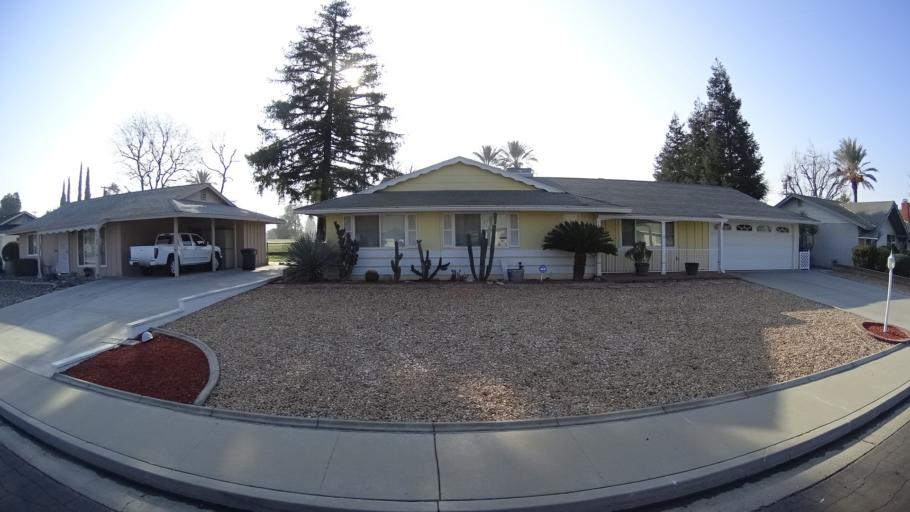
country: US
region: California
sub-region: Kern County
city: Greenacres
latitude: 35.3491
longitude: -119.0684
